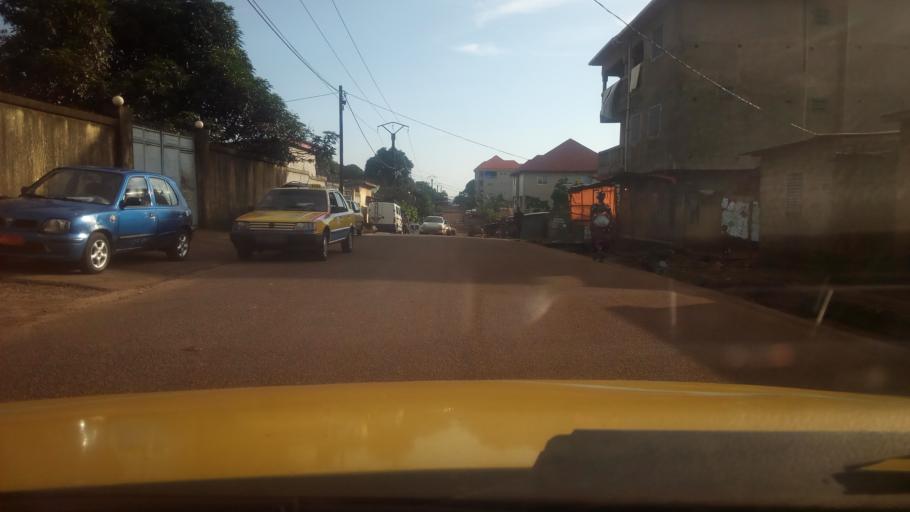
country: GN
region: Conakry
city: Conakry
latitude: 9.6189
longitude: -13.6086
